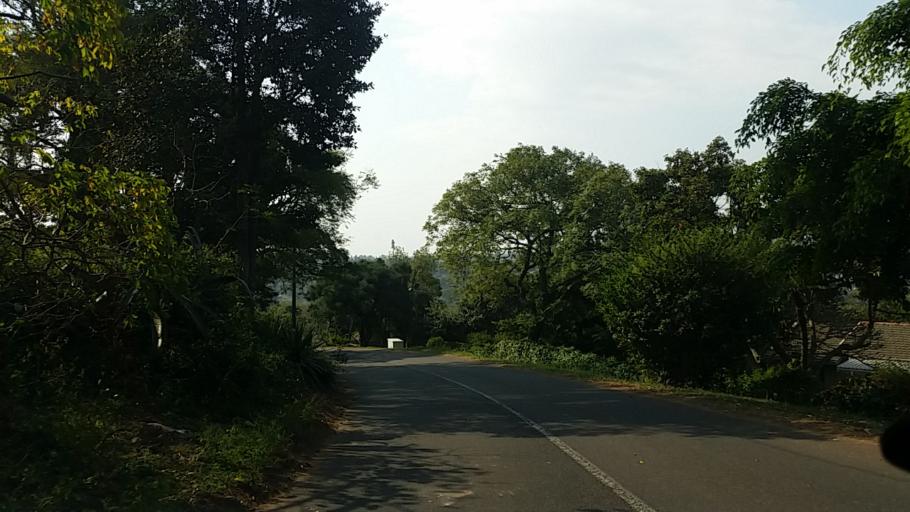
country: ZA
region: KwaZulu-Natal
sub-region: eThekwini Metropolitan Municipality
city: Berea
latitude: -29.8426
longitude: 30.9479
